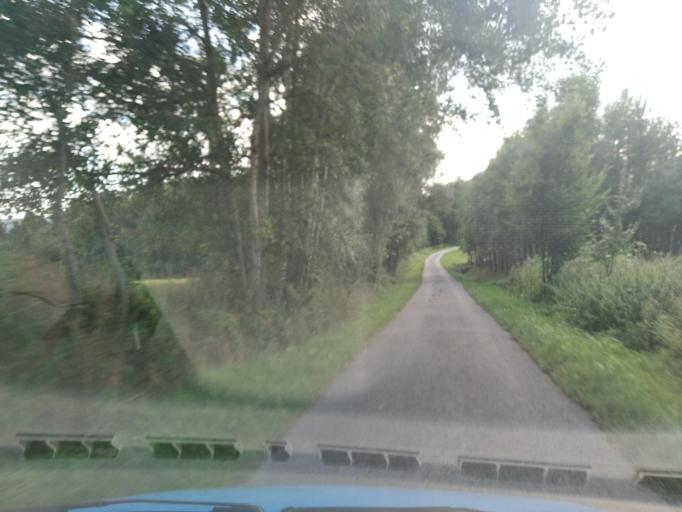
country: PL
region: Subcarpathian Voivodeship
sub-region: Powiat strzyzowski
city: Polomia
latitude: 49.8938
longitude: 21.9085
